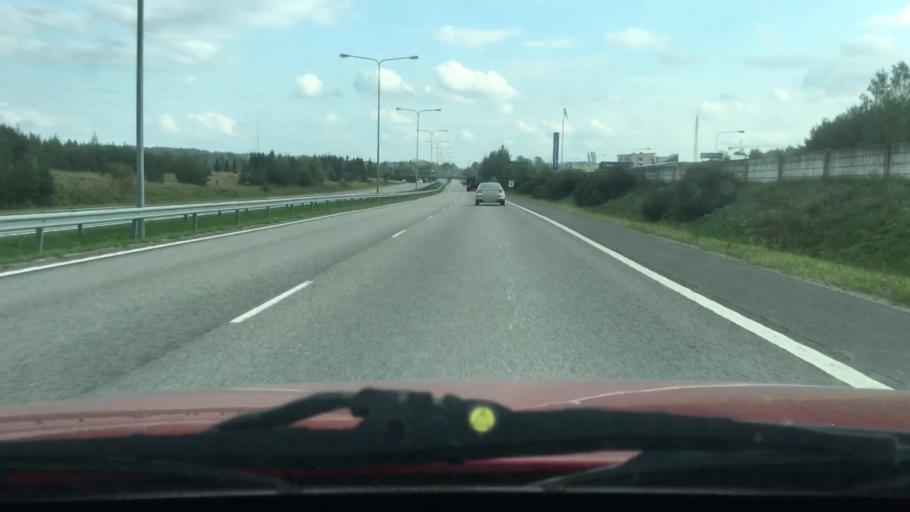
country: FI
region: Varsinais-Suomi
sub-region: Turku
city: Raisio
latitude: 60.4935
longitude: 22.1678
